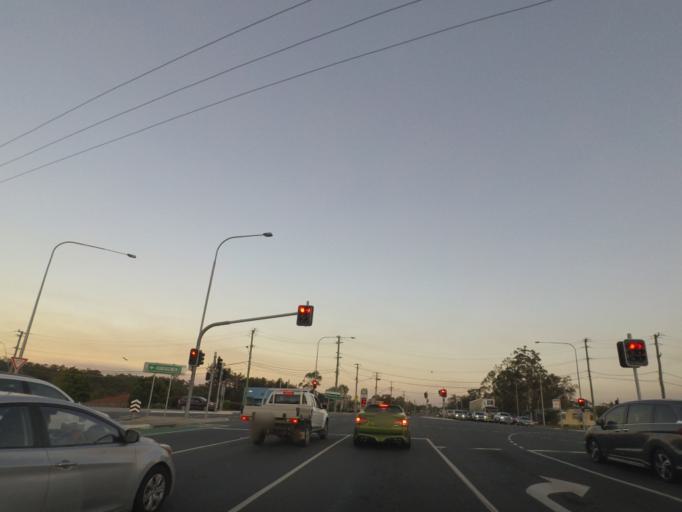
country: AU
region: Queensland
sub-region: Brisbane
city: Mackenzie
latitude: -27.5454
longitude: 153.1205
